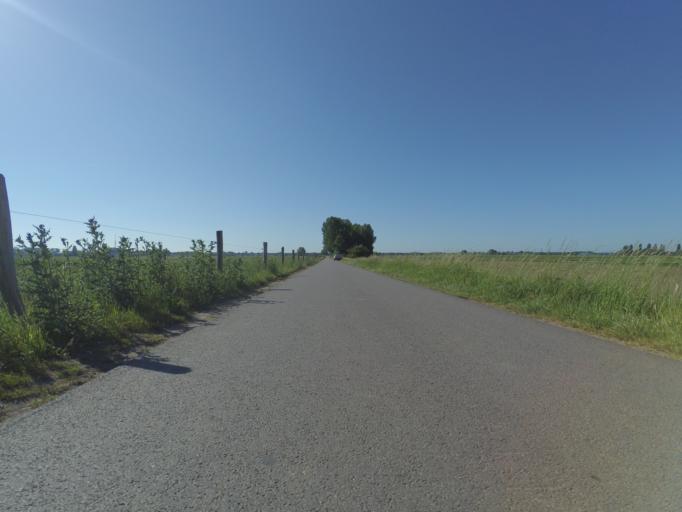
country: NL
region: Overijssel
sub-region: Gemeente Deventer
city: Deventer
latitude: 52.2426
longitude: 6.1576
